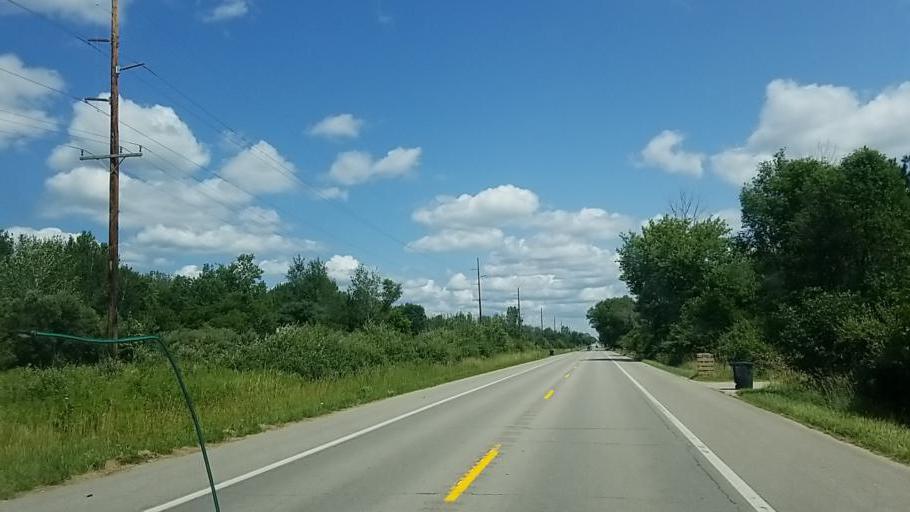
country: US
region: Michigan
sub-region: Newaygo County
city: Fremont
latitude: 43.4236
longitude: -85.9089
